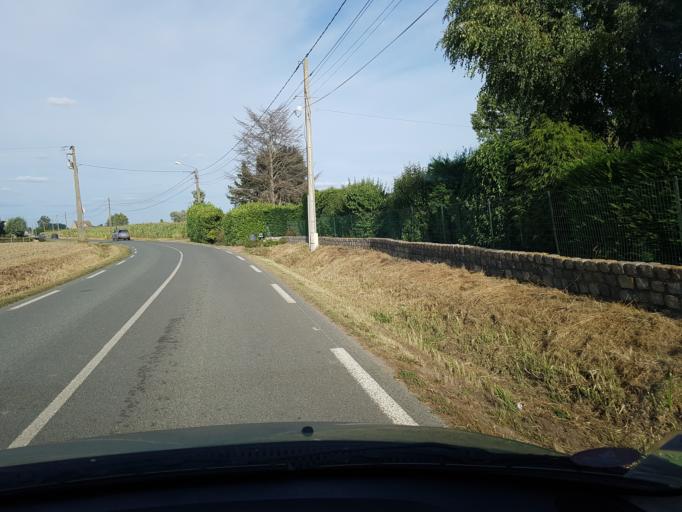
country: FR
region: Nord-Pas-de-Calais
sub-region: Departement du Pas-de-Calais
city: Richebourg-l'Avoue
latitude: 50.5945
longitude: 2.7483
